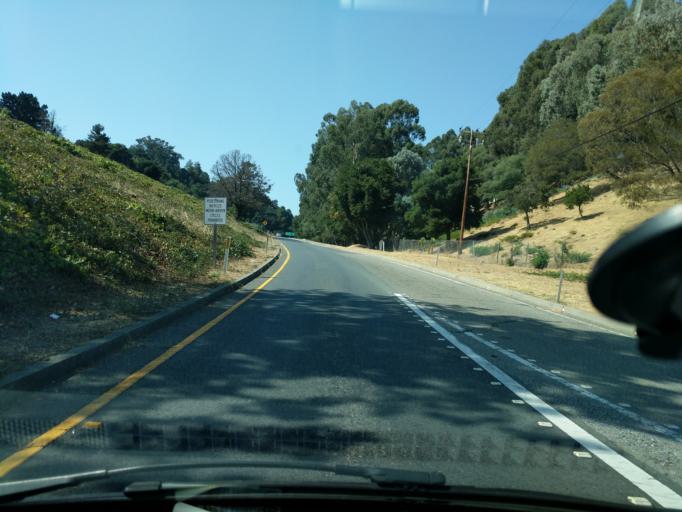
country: US
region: California
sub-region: Alameda County
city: San Leandro
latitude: 37.7852
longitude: -122.1781
